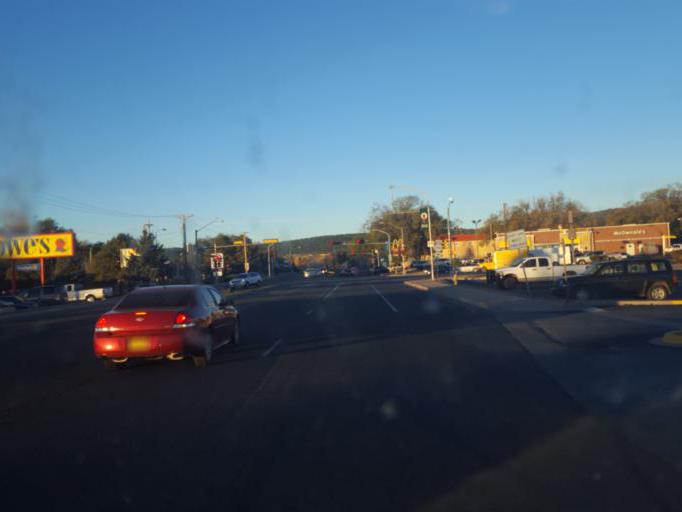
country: US
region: New Mexico
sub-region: San Miguel County
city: Las Vegas
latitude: 35.6060
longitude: -105.2220
